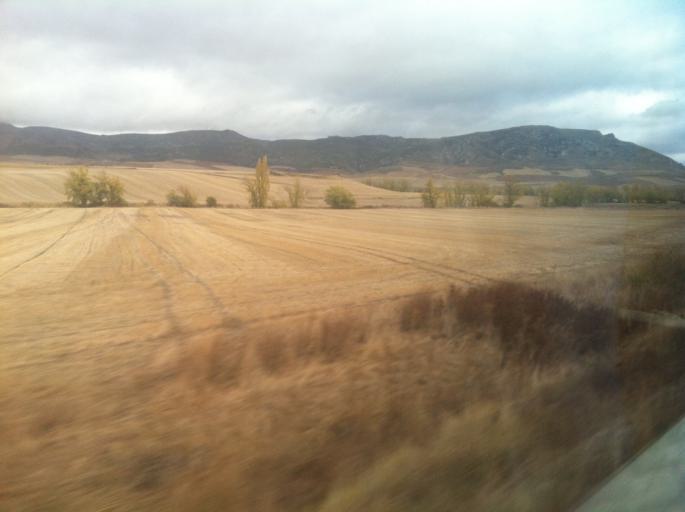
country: ES
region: Castille and Leon
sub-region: Provincia de Burgos
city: Villanueva de Teba
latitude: 42.6239
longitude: -3.1646
